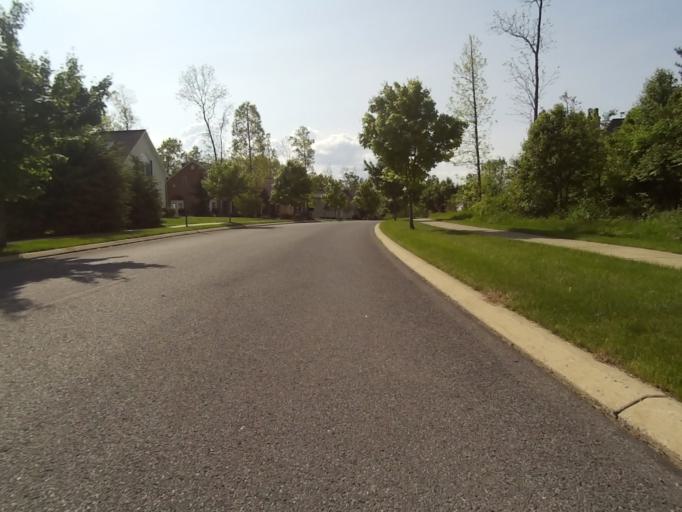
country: US
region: Pennsylvania
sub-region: Centre County
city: Houserville
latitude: 40.8250
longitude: -77.8201
